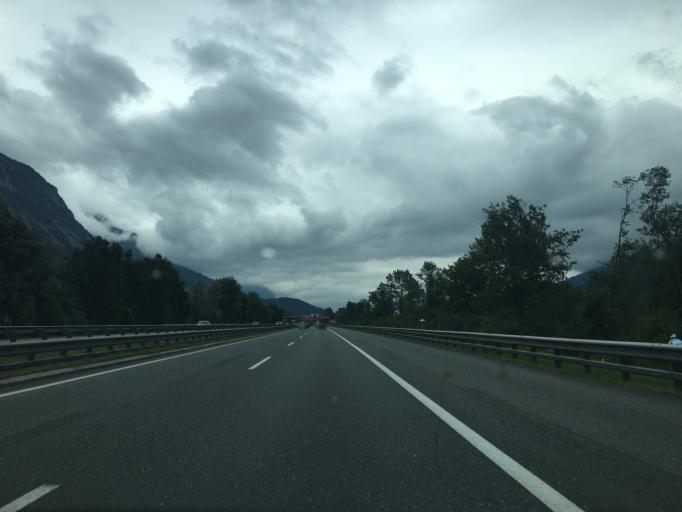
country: AT
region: Tyrol
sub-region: Politischer Bezirk Schwaz
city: Stans
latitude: 47.3676
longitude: 11.7322
